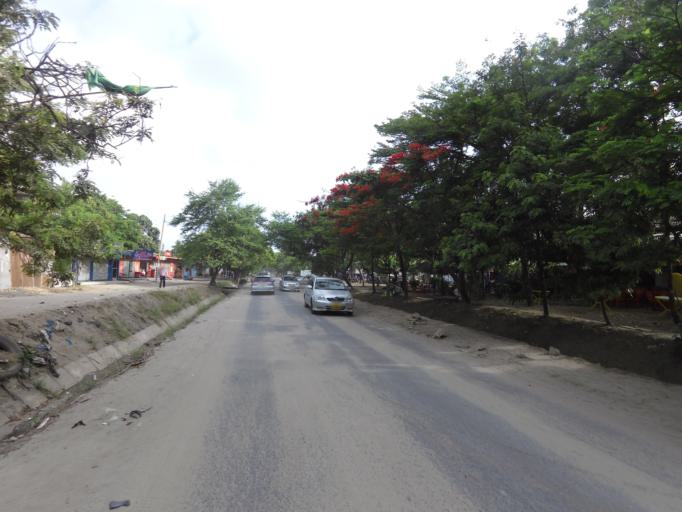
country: TZ
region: Dar es Salaam
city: Magomeni
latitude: -6.7779
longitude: 39.2412
